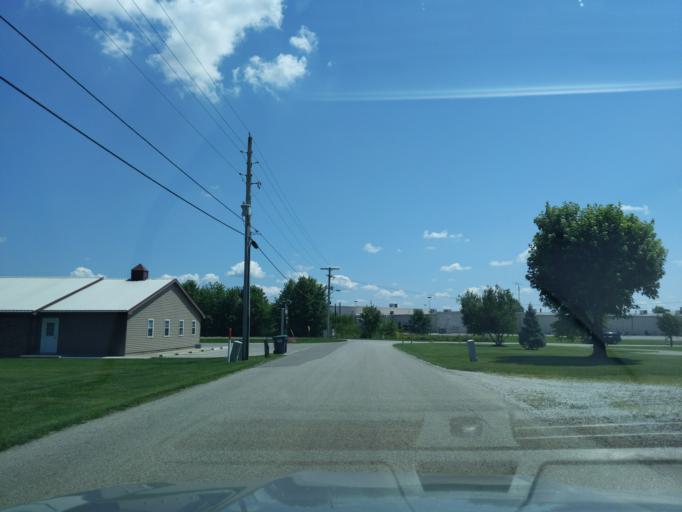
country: US
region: Indiana
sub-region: Decatur County
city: Greensburg
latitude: 39.3566
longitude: -85.4854
